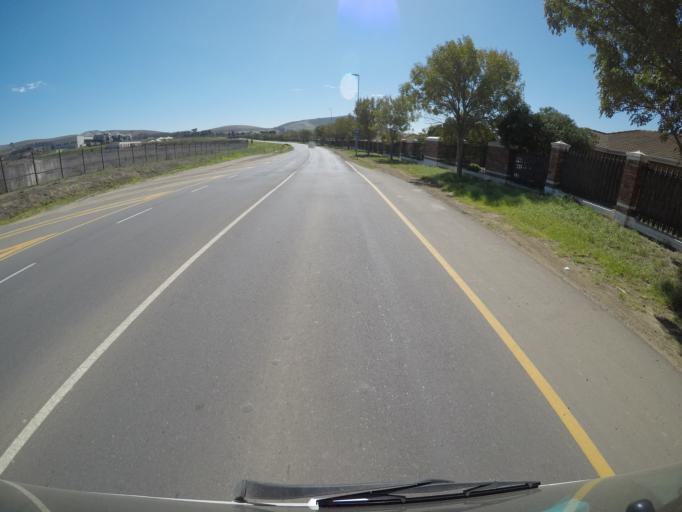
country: ZA
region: Western Cape
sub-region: City of Cape Town
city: Kraaifontein
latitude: -33.8169
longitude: 18.6341
